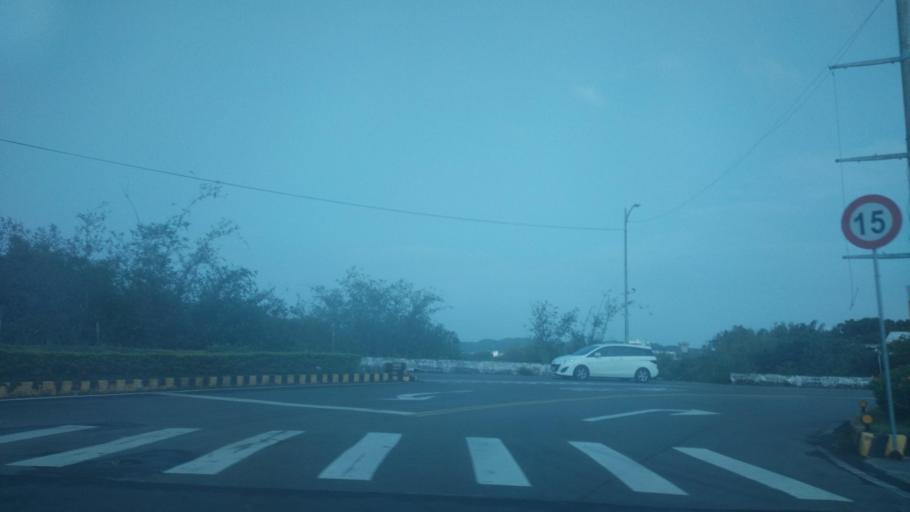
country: TW
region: Taiwan
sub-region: Keelung
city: Keelung
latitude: 25.2289
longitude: 121.6299
